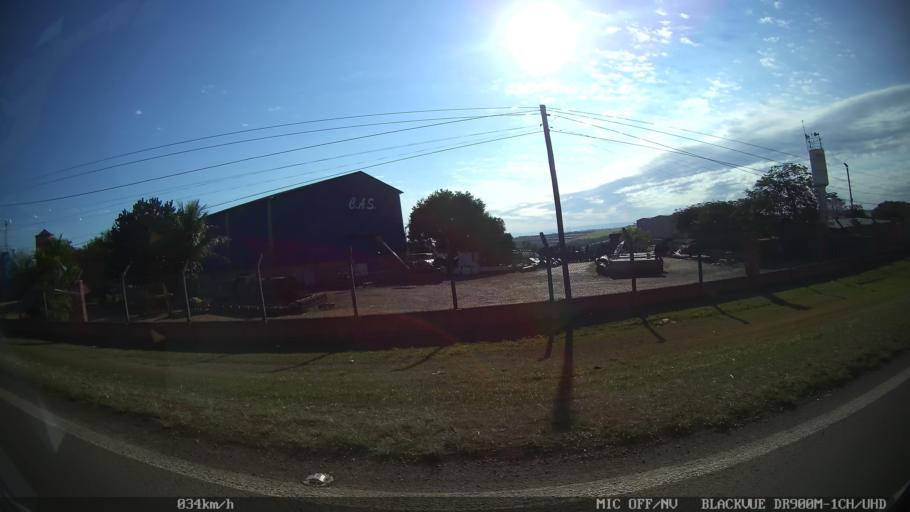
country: BR
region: Sao Paulo
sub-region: Piracicaba
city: Piracicaba
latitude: -22.6638
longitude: -47.6187
